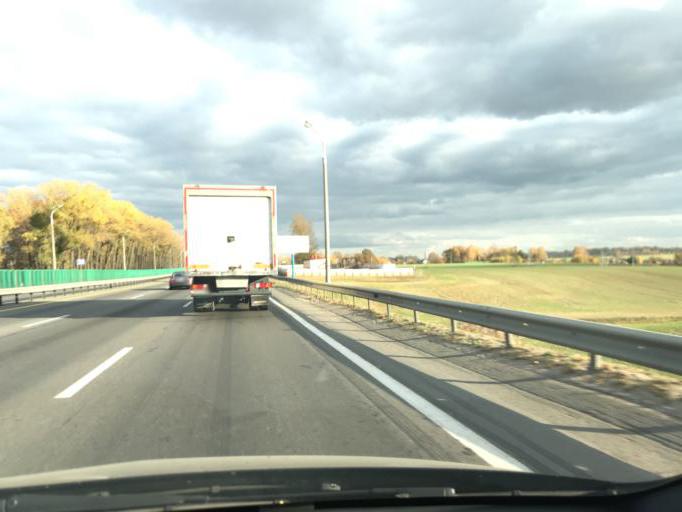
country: BY
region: Minsk
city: Syenitsa
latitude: 53.8342
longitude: 27.5430
